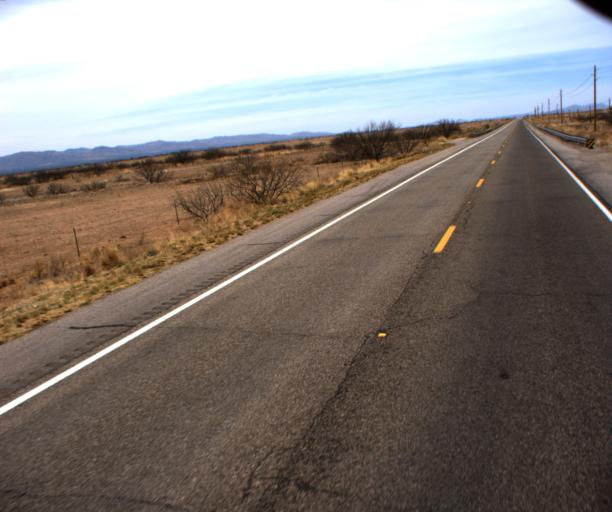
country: US
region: Arizona
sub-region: Cochise County
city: Pirtleville
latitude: 31.4403
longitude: -109.5947
